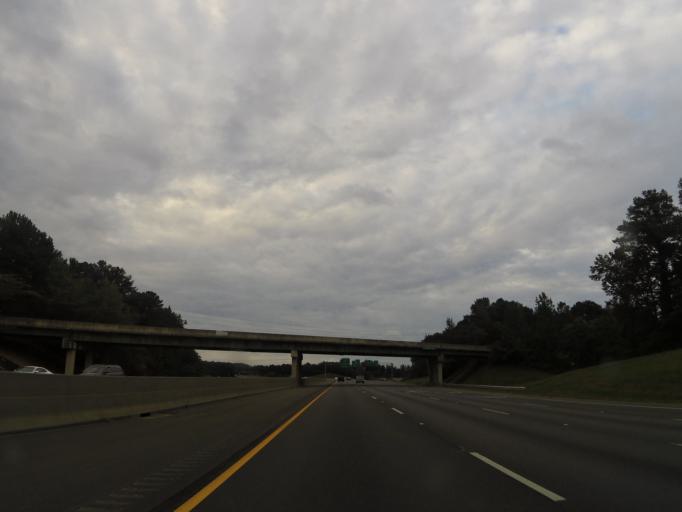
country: US
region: Alabama
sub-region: Jefferson County
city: Trussville
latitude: 33.5669
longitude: -86.6385
